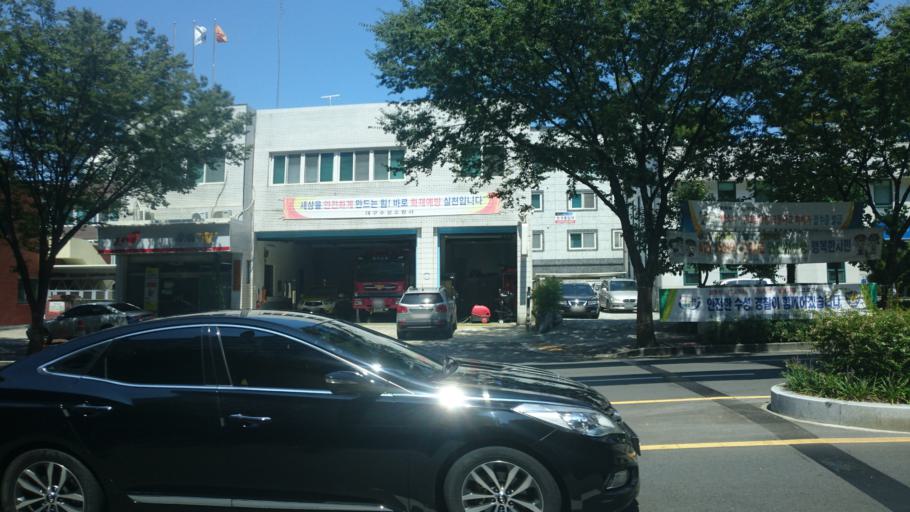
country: KR
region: Daegu
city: Daegu
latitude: 35.8229
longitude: 128.6367
